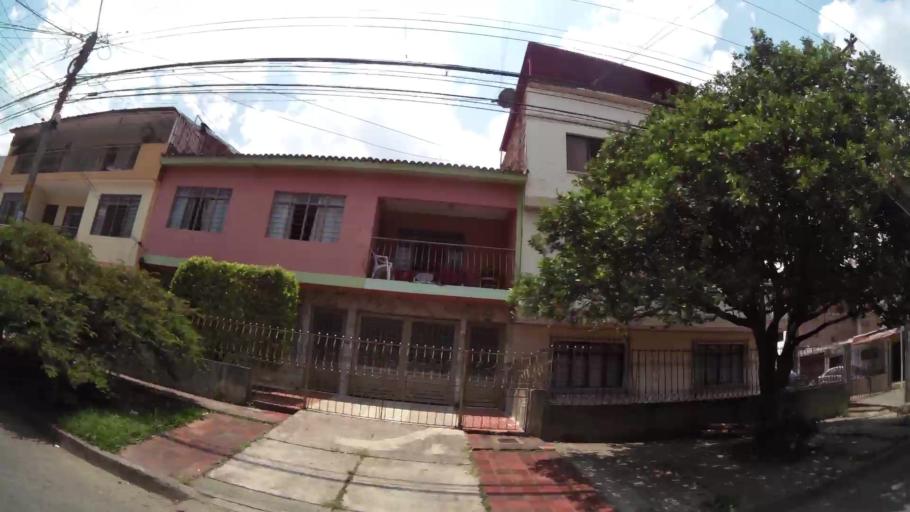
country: CO
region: Valle del Cauca
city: Cali
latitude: 3.4139
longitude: -76.5351
